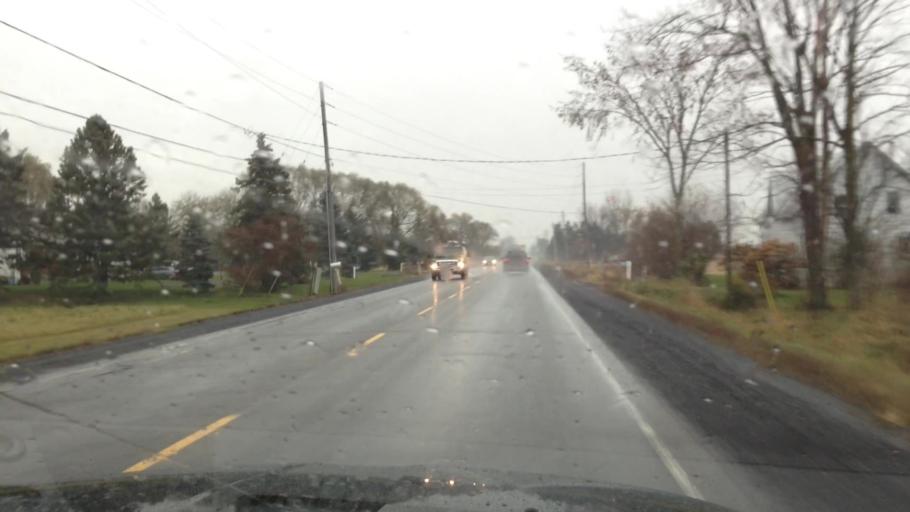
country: CA
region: Ontario
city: Bourget
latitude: 45.3097
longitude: -75.3339
